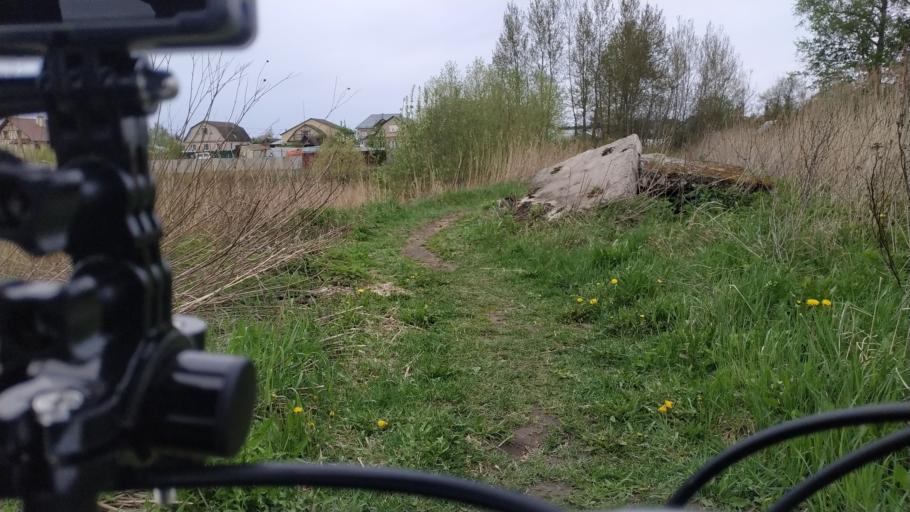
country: RU
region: Moskovskaya
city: Malyshevo
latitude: 55.5539
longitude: 38.3133
